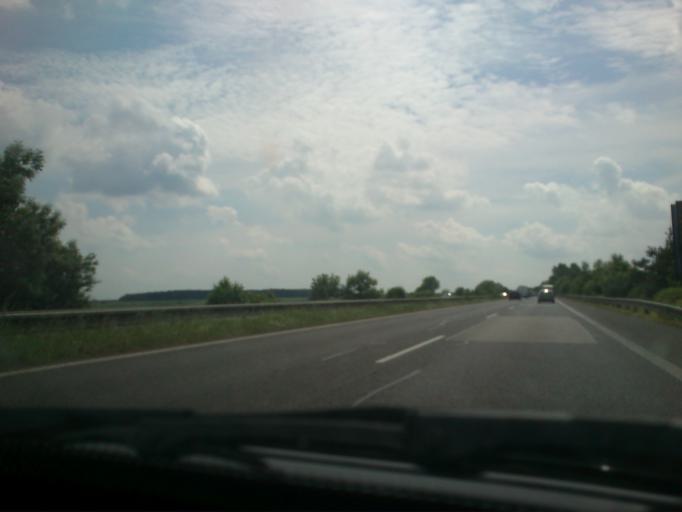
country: CZ
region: Central Bohemia
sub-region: Okres Mlada Boleslav
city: Mlada Boleslav
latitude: 50.3720
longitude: 14.8837
